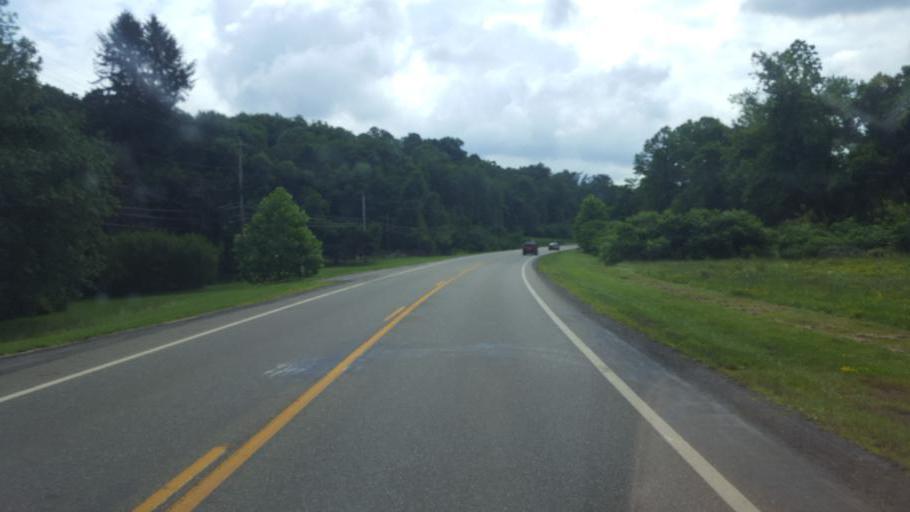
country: US
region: Ohio
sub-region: Columbiana County
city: Lisbon
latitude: 40.7720
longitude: -80.7515
